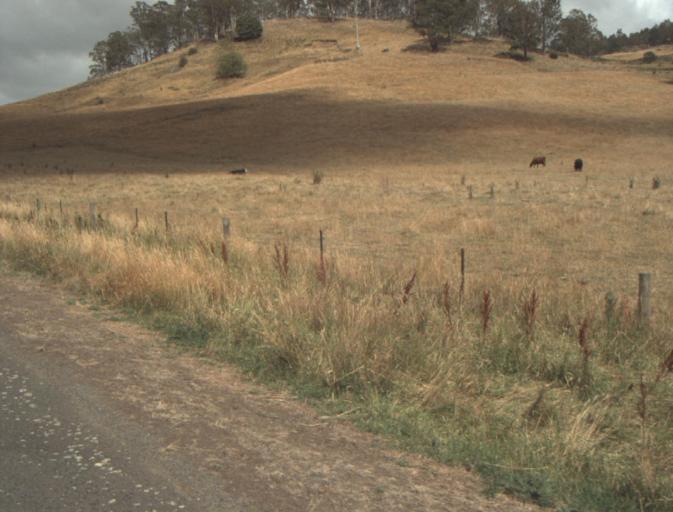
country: AU
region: Tasmania
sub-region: Northern Midlands
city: Evandale
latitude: -41.5176
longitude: 147.4711
